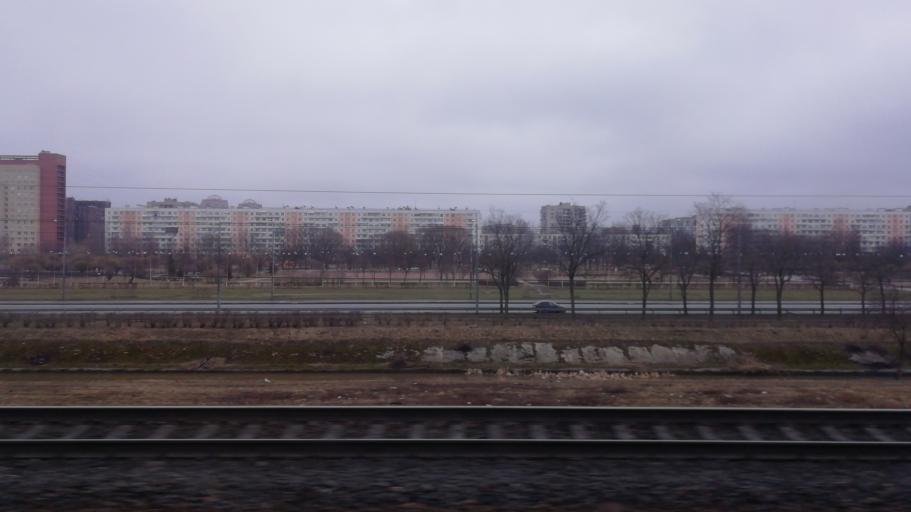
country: RU
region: St.-Petersburg
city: Kupchino
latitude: 59.8636
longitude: 30.3596
